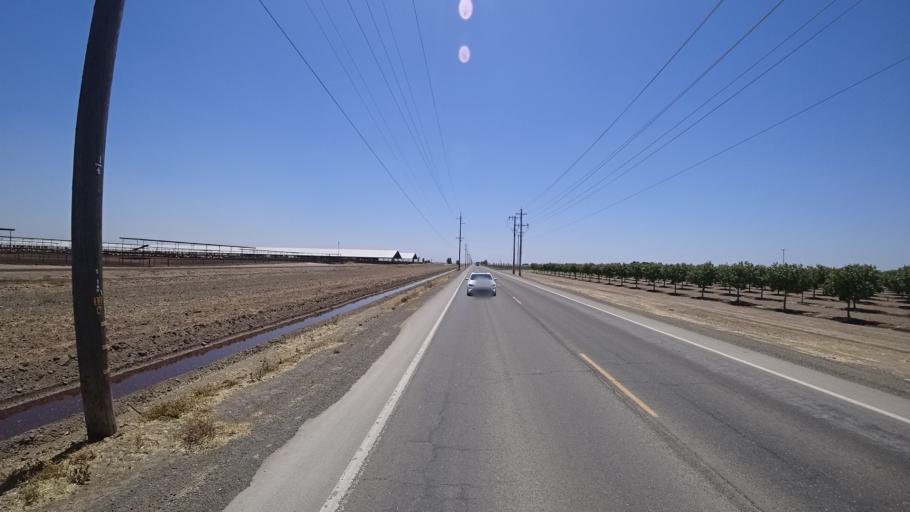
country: US
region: California
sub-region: Kings County
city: Home Garden
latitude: 36.2015
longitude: -119.6459
